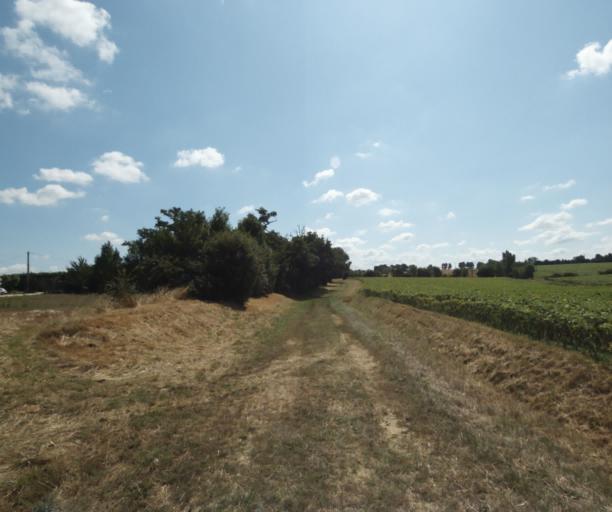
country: FR
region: Midi-Pyrenees
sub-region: Departement de la Haute-Garonne
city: Auriac-sur-Vendinelle
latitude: 43.4644
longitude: 1.8059
